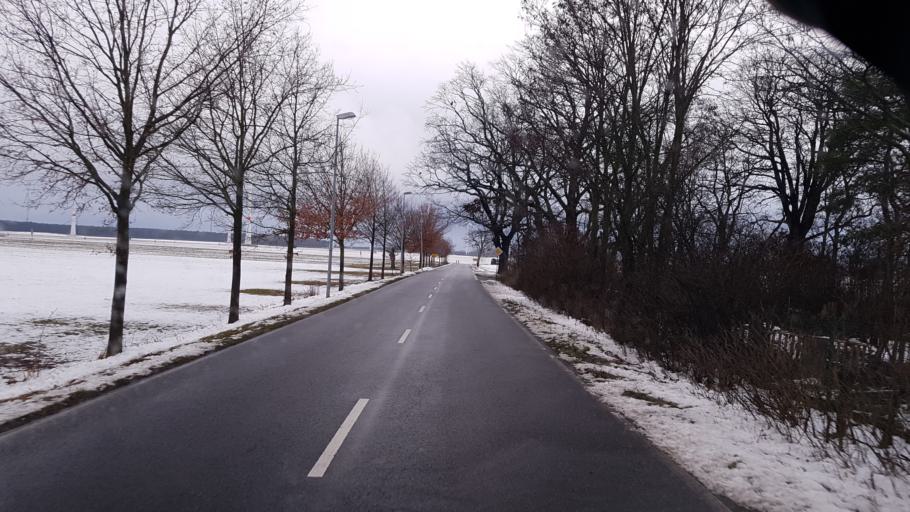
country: DE
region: Brandenburg
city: Luckau
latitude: 51.8838
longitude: 13.7872
